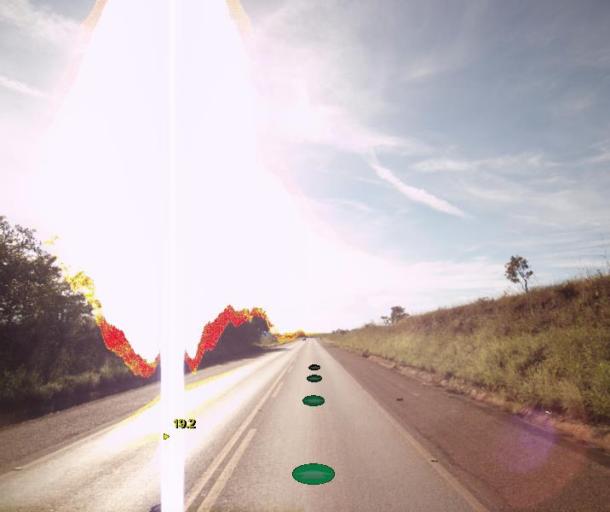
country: BR
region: Federal District
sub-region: Brasilia
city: Brasilia
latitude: -15.7434
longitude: -48.3678
